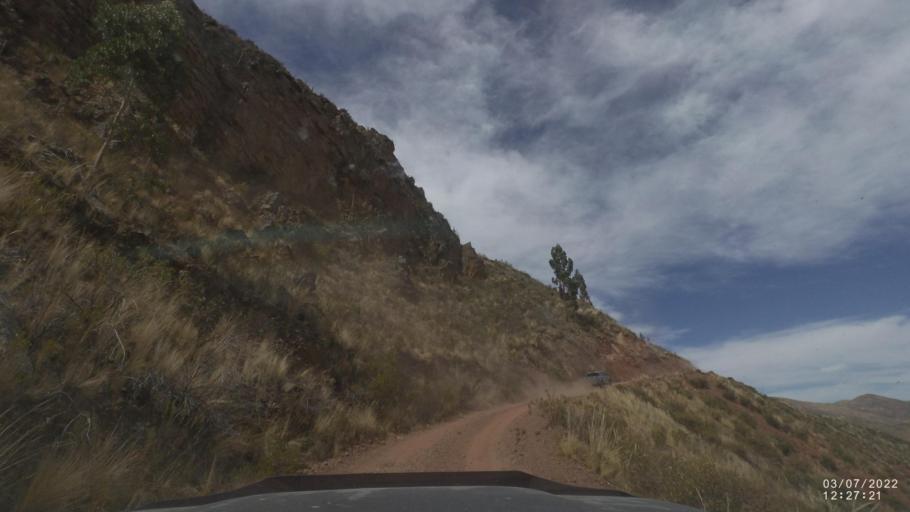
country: BO
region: Cochabamba
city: Irpa Irpa
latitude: -17.8109
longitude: -66.6140
